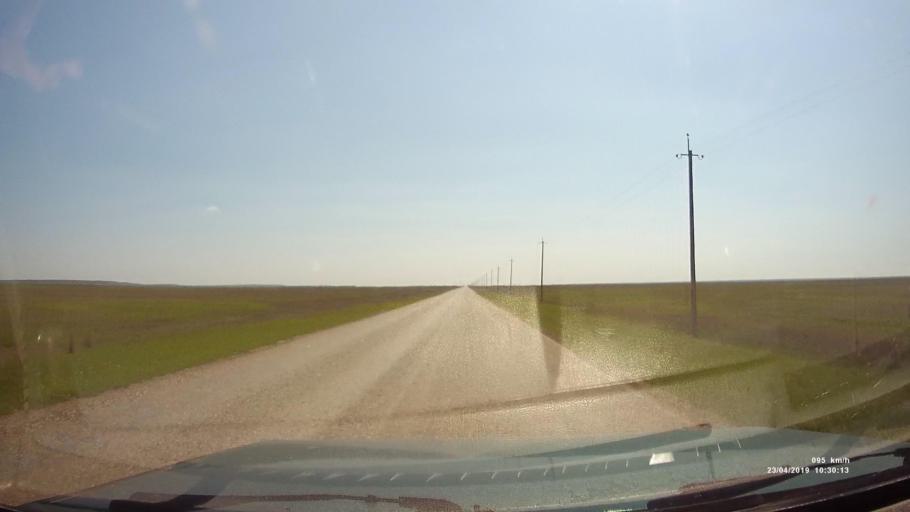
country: RU
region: Kalmykiya
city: Yashalta
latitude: 46.5936
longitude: 42.5405
